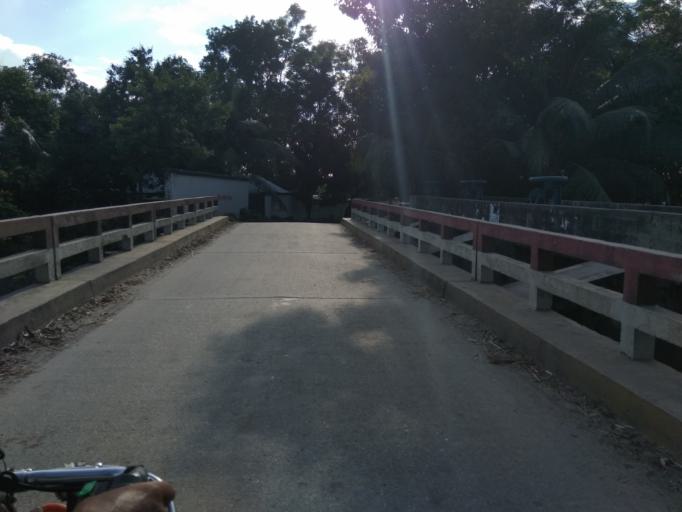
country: BD
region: Rangpur Division
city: Rangpur
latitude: 25.8325
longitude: 89.1133
